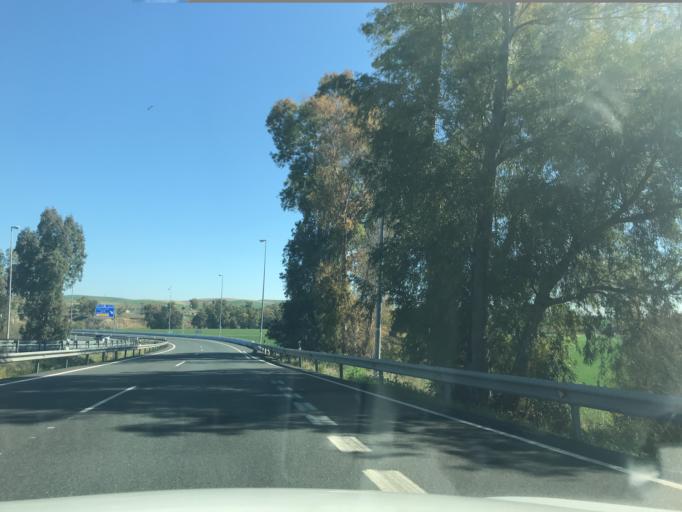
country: ES
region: Andalusia
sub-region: Province of Cordoba
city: Cordoba
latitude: 37.8119
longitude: -4.7985
